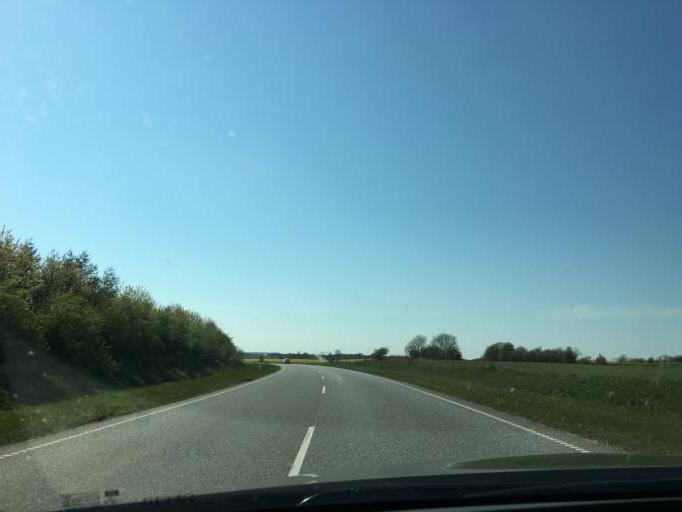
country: DK
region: South Denmark
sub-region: Kolding Kommune
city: Kolding
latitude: 55.5467
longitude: 9.4705
